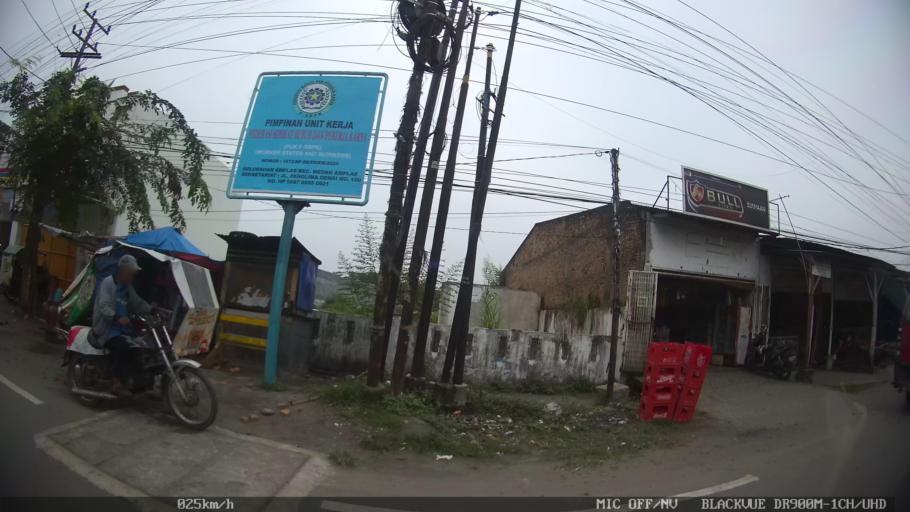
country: ID
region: North Sumatra
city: Deli Tua
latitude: 3.5499
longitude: 98.7152
